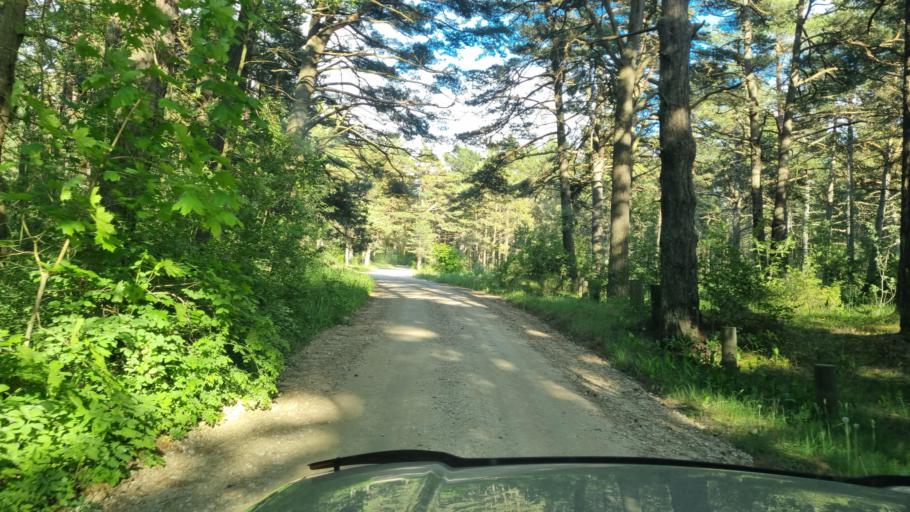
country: LV
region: Ventspils
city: Ventspils
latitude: 57.3676
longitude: 21.5172
